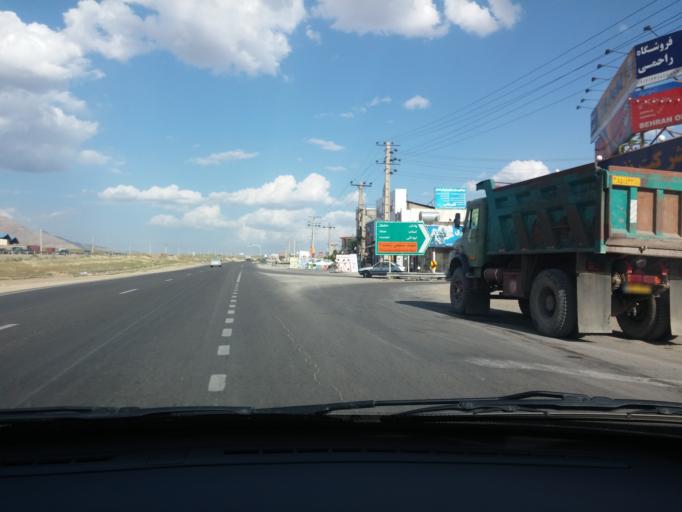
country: IR
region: Tehran
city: Damavand
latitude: 35.6737
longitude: 52.0698
